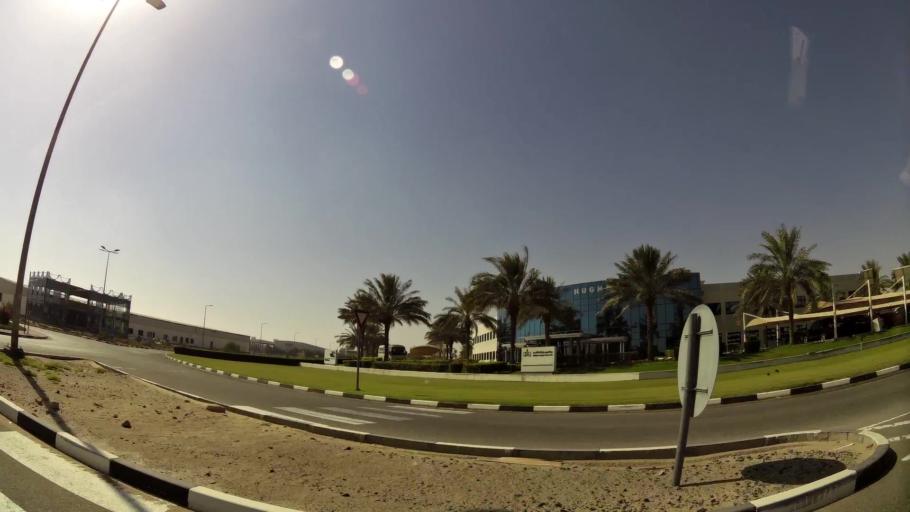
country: AE
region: Dubai
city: Dubai
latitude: 24.9390
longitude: 55.0568
